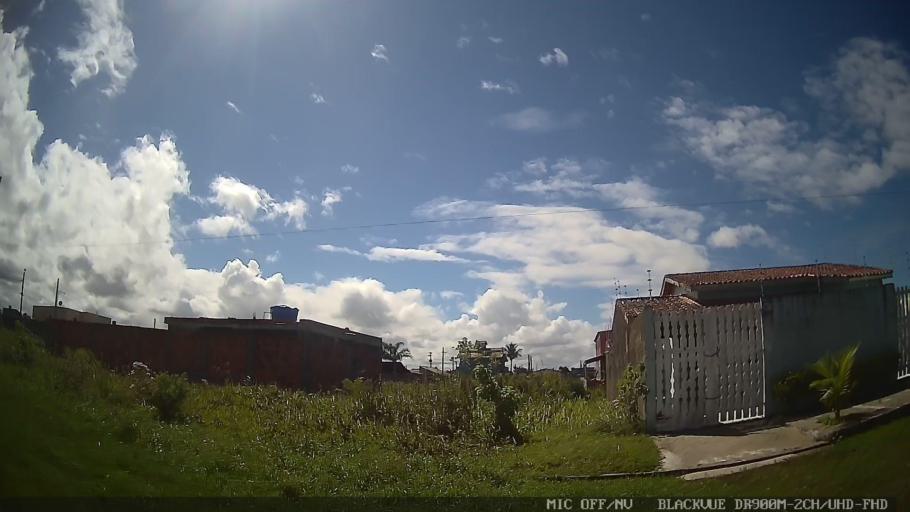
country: BR
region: Sao Paulo
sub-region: Itanhaem
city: Itanhaem
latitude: -24.2273
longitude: -46.8827
